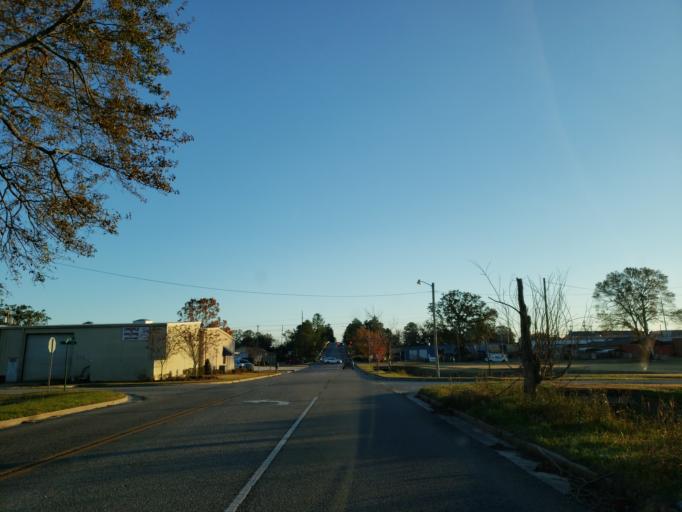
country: US
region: Georgia
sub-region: Crisp County
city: Cordele
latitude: 31.9733
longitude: -83.7797
